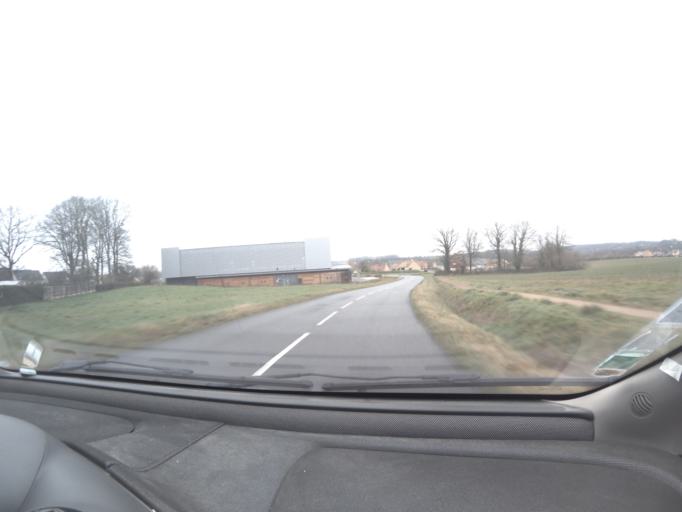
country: FR
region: Pays de la Loire
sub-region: Departement de la Sarthe
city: Saint-Saturnin
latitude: 48.0584
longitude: 0.1446
